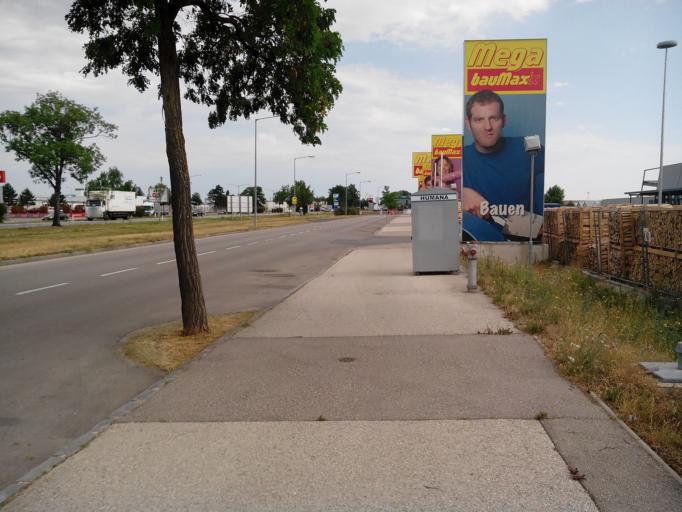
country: AT
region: Lower Austria
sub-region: Politischer Bezirk Wiener Neustadt
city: Theresienfeld
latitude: 47.8405
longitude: 16.2460
